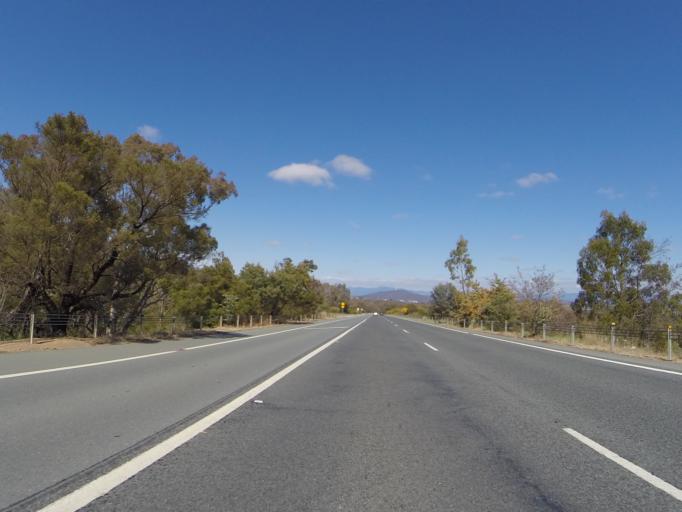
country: AU
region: Australian Capital Territory
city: Kaleen
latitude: -35.2170
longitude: 149.1832
